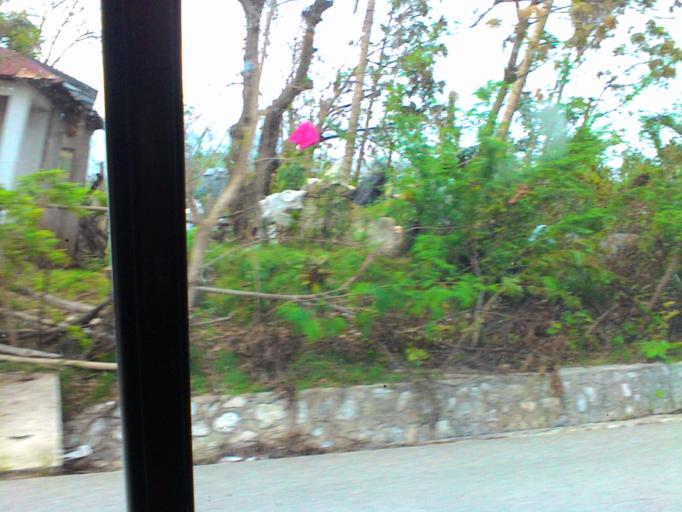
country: HT
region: Sud
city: Chantal
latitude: 18.3382
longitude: -73.8441
